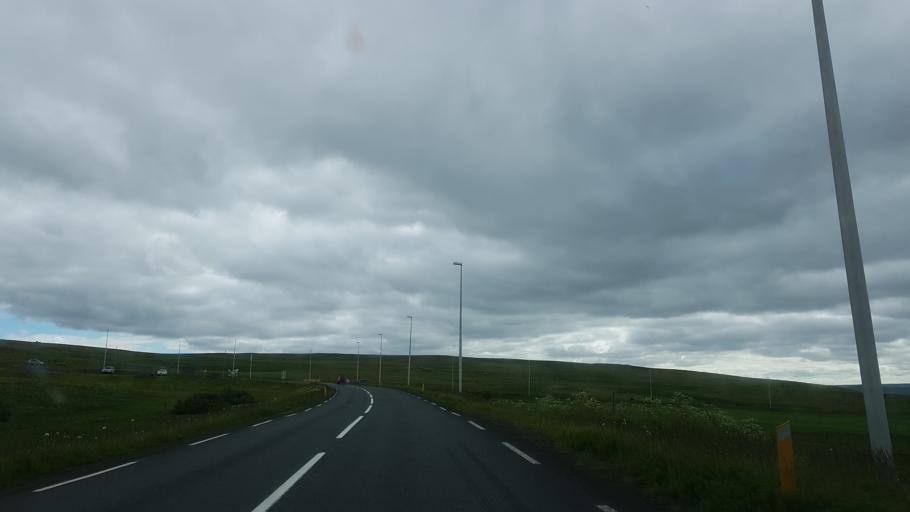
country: IS
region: Northwest
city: Saudarkrokur
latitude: 65.3539
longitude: -20.8870
